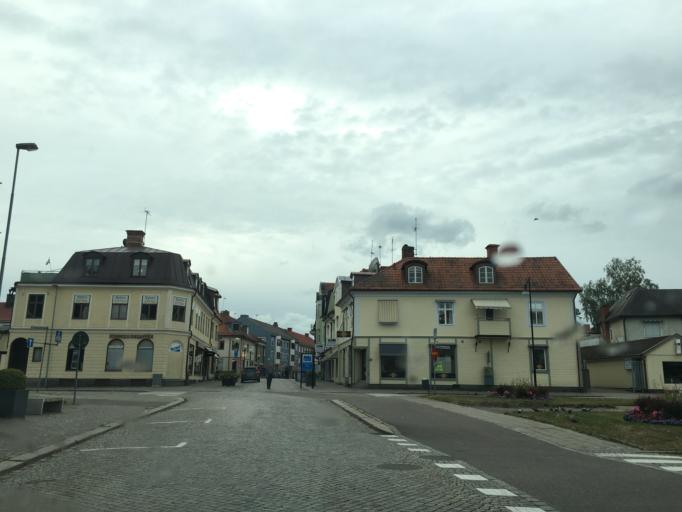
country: SE
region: Kalmar
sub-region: Nybro Kommun
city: Nybro
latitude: 56.7443
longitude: 15.9110
